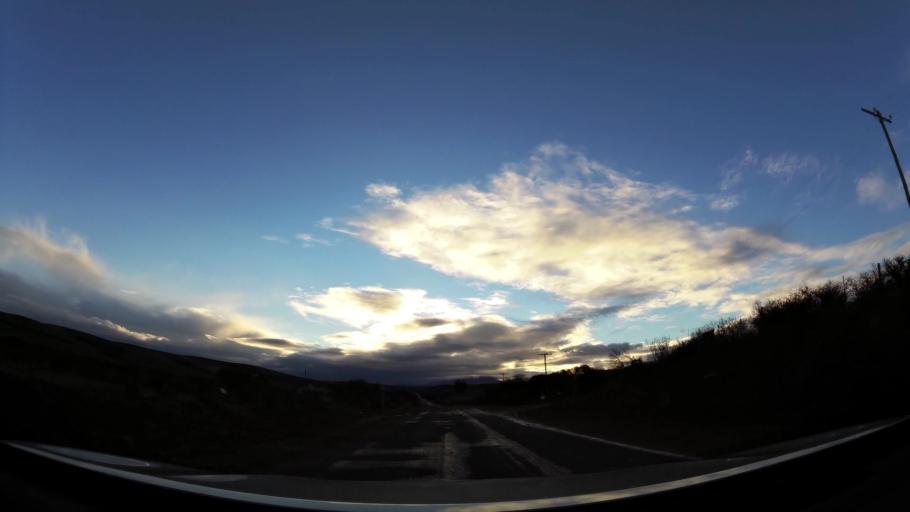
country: ZA
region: Western Cape
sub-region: Eden District Municipality
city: Riversdale
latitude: -34.0633
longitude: 20.8862
